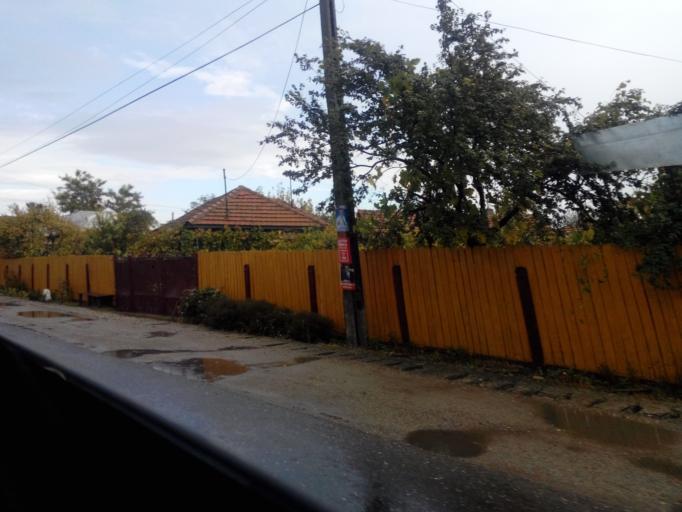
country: RO
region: Buzau
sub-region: Comuna Costesti
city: Pietrosu
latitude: 45.0880
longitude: 26.7772
